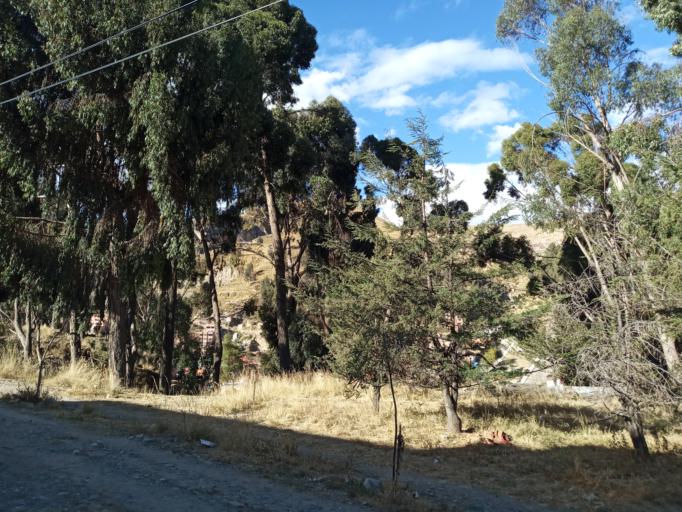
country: BO
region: La Paz
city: La Paz
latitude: -16.4591
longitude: -68.1491
